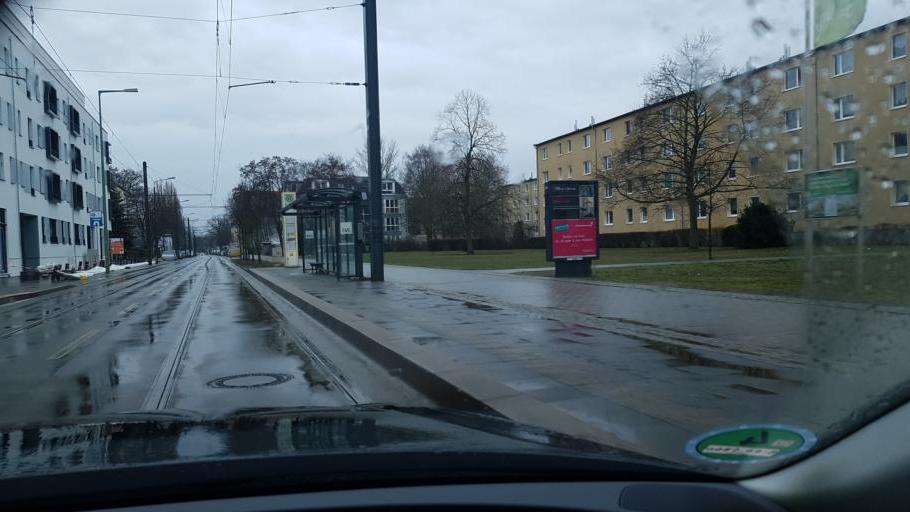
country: DE
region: Berlin
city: Grunau
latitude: 52.4246
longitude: 13.5750
